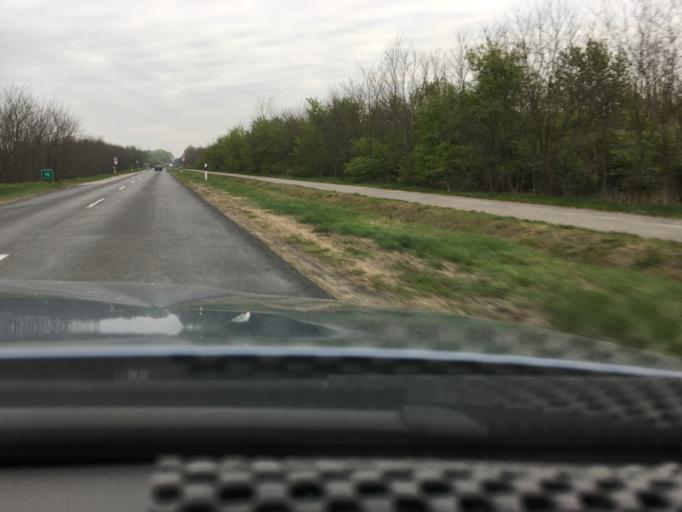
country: HU
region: Hajdu-Bihar
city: Hajdusamson
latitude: 47.6269
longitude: 21.7886
